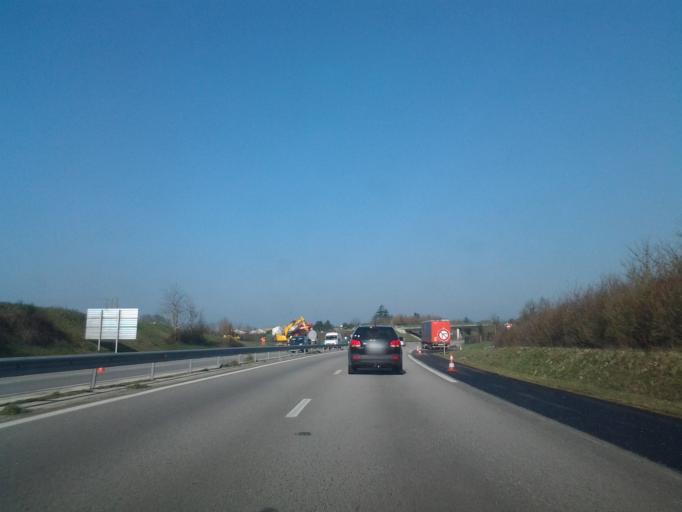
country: FR
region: Pays de la Loire
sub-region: Departement de la Vendee
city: Aizenay
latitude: 46.7357
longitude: -1.6181
